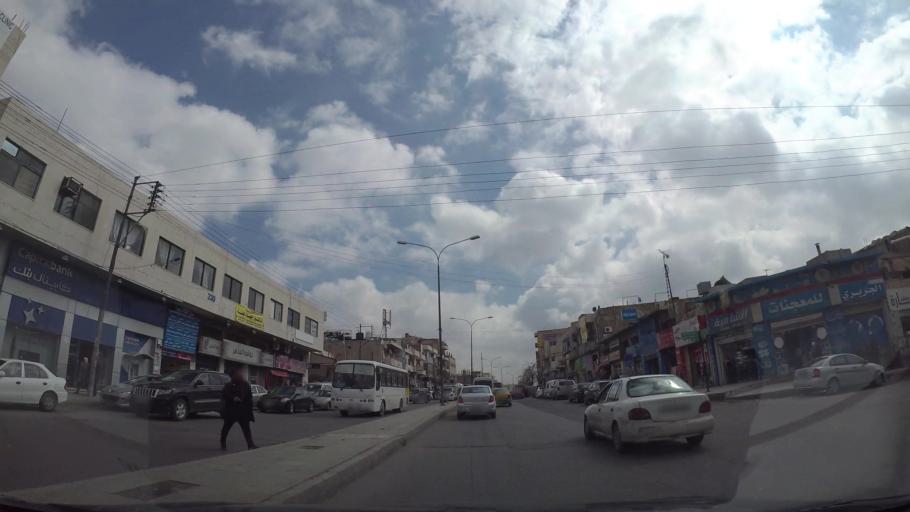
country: JO
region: Amman
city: Al Quwaysimah
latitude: 31.9286
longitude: 35.9373
